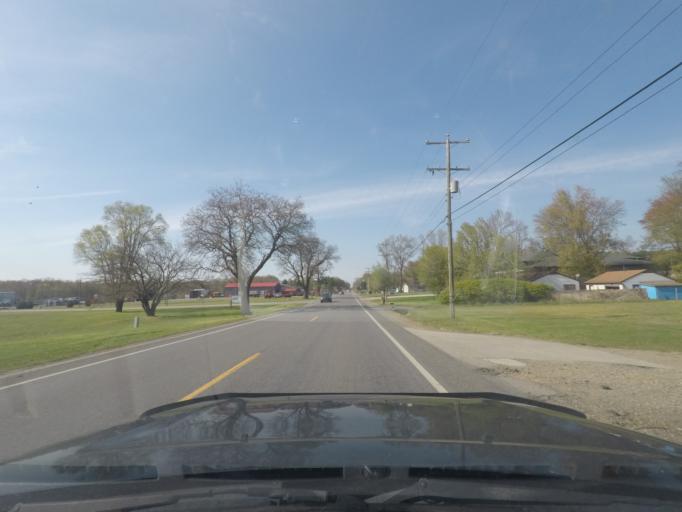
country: US
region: Michigan
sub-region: Berrien County
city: Niles
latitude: 41.7927
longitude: -86.2547
